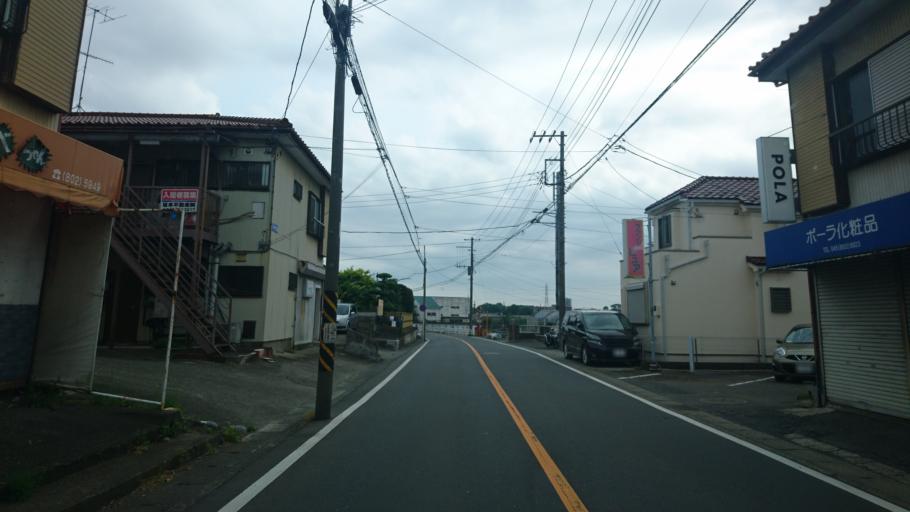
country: JP
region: Kanagawa
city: Fujisawa
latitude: 35.4145
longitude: 139.4793
